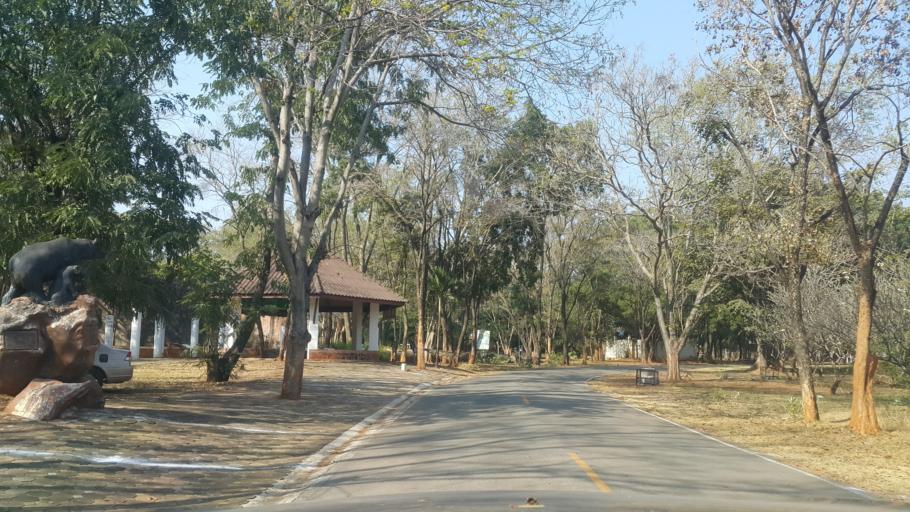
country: TH
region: Nakhon Ratchasima
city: Nakhon Ratchasima
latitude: 14.8521
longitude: 102.0826
